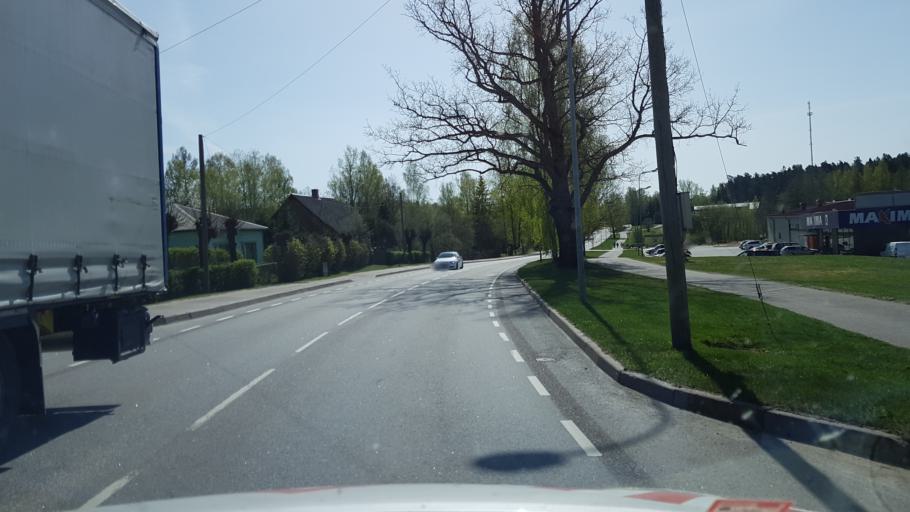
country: EE
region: Valgamaa
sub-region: Torva linn
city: Torva
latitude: 57.9988
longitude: 25.9321
